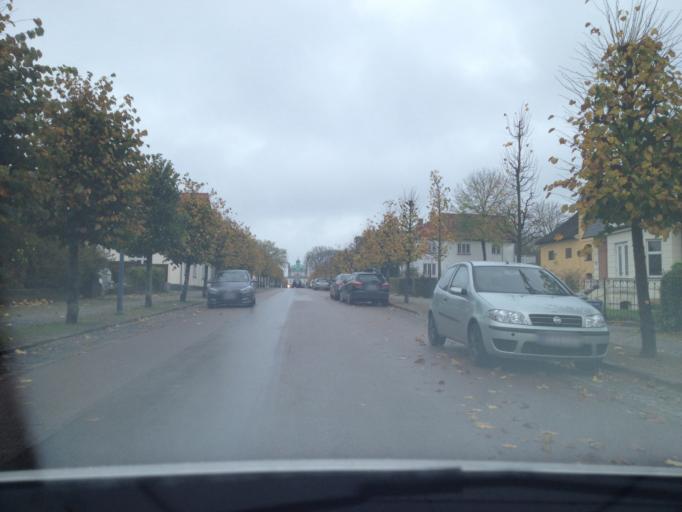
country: DK
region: Capital Region
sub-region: Fredensborg Kommune
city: Fredensborg
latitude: 55.9769
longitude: 12.3965
